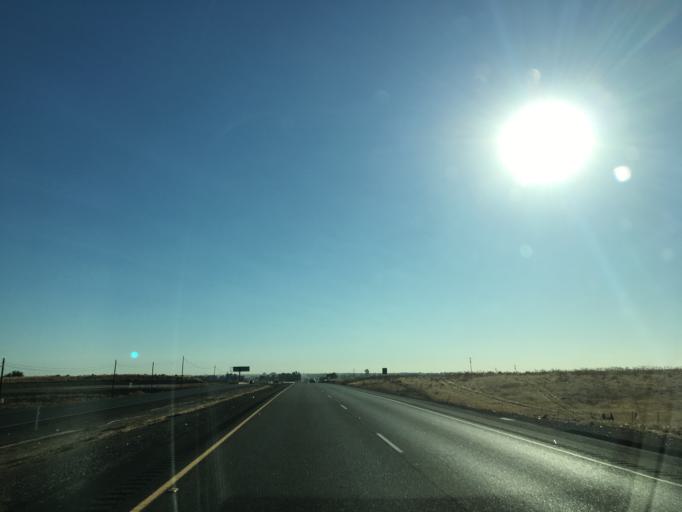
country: US
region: California
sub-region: Merced County
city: Los Banos
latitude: 37.0566
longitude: -120.9506
